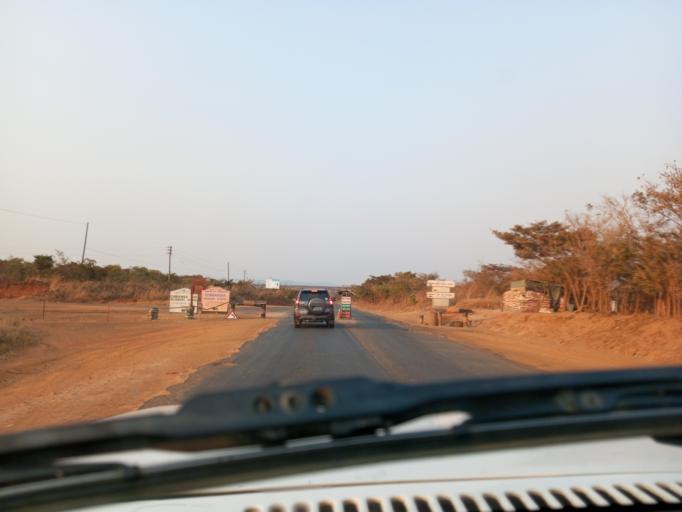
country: ZM
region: Northern
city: Mpika
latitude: -11.8934
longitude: 31.4176
